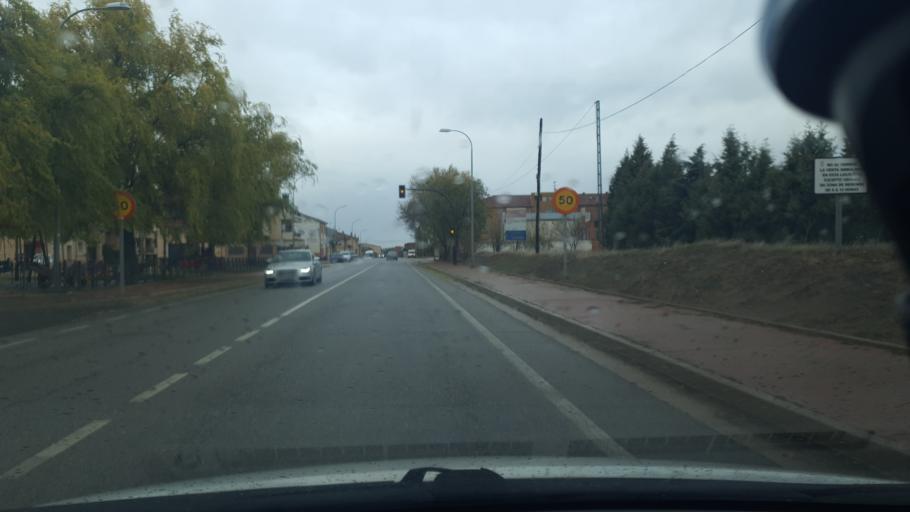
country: ES
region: Castille and Leon
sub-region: Provincia de Segovia
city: Carbonero el Mayor
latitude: 41.1154
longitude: -4.2611
